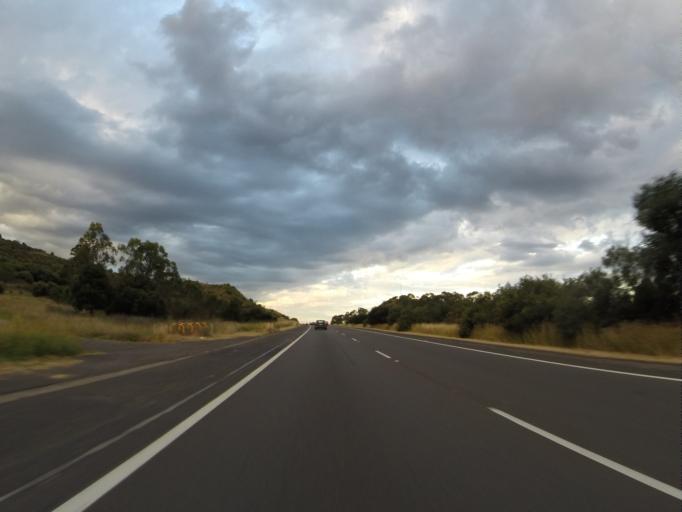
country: AU
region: New South Wales
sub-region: Wollondilly
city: Douglas Park
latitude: -34.1756
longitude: 150.7298
